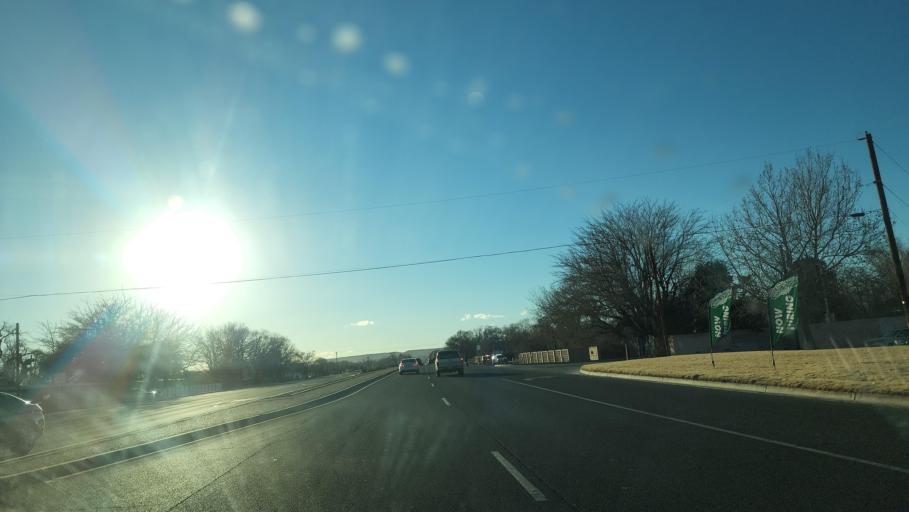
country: US
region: New Mexico
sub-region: Bernalillo County
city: South Valley
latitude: 35.0269
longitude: -106.6825
